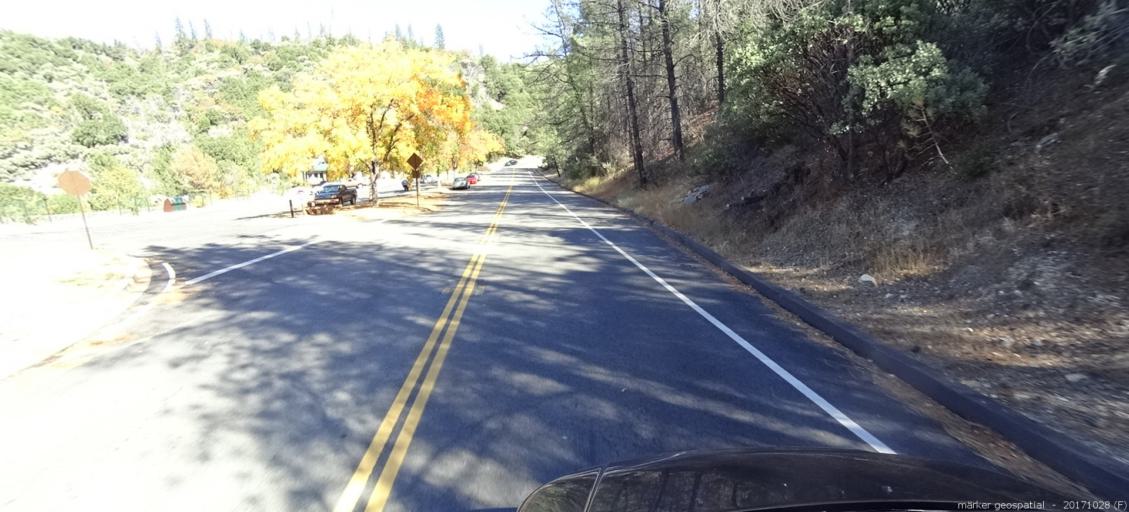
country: US
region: California
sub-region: Shasta County
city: Shasta
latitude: 40.6141
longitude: -122.5208
